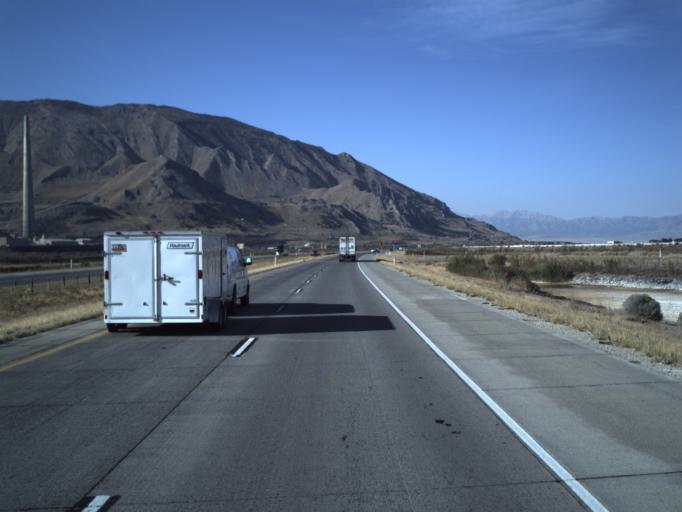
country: US
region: Utah
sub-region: Salt Lake County
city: Magna
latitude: 40.7442
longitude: -112.1846
